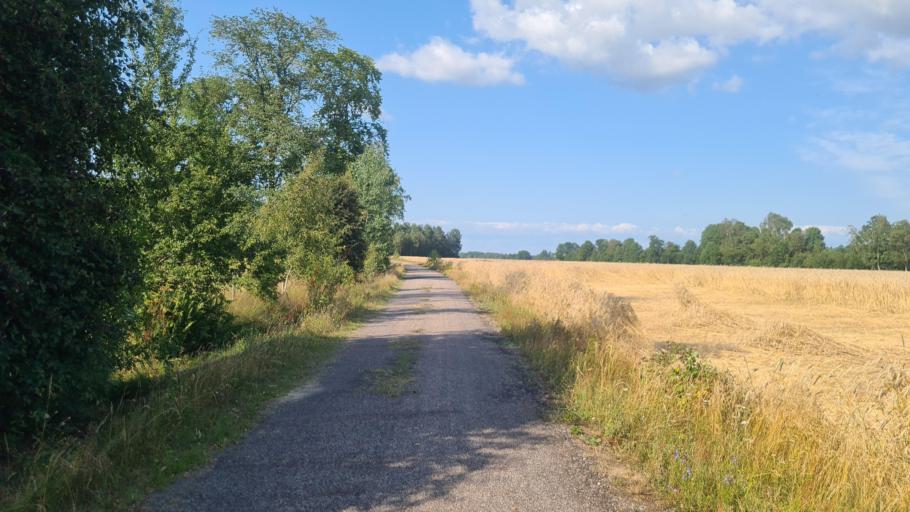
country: SE
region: Kronoberg
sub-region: Ljungby Kommun
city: Ljungby
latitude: 56.8015
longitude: 13.9142
